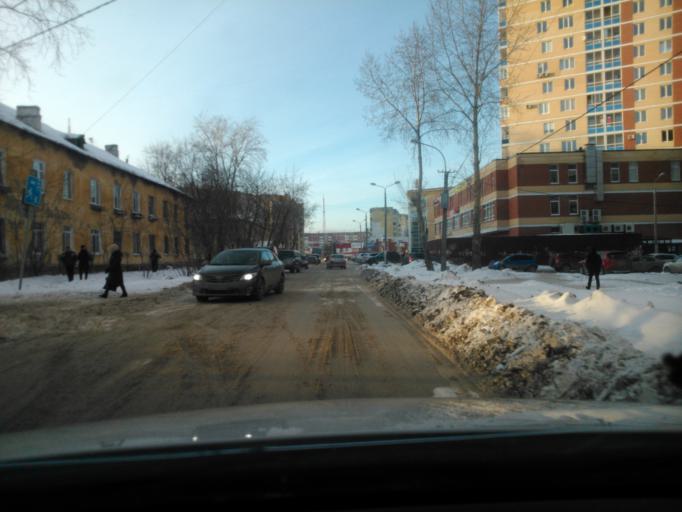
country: RU
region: Perm
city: Perm
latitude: 58.0007
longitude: 56.3046
